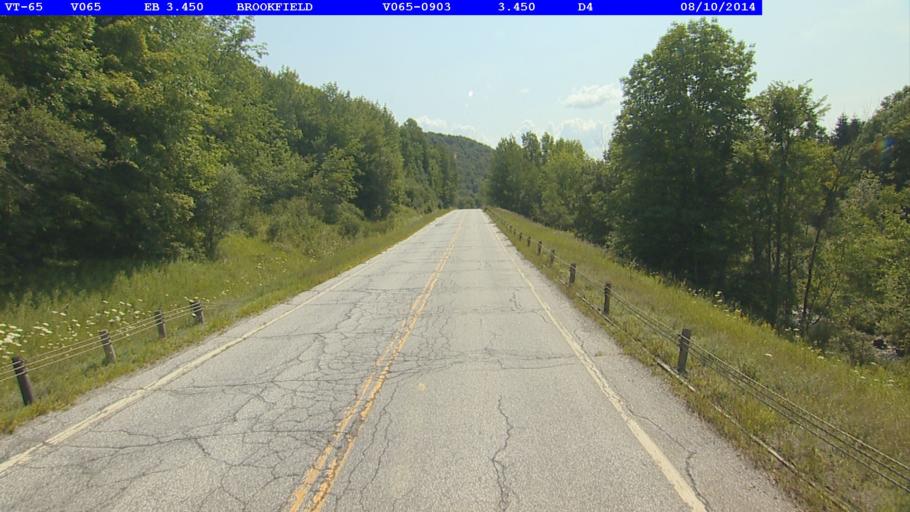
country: US
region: Vermont
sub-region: Orange County
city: Williamstown
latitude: 44.0387
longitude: -72.5975
